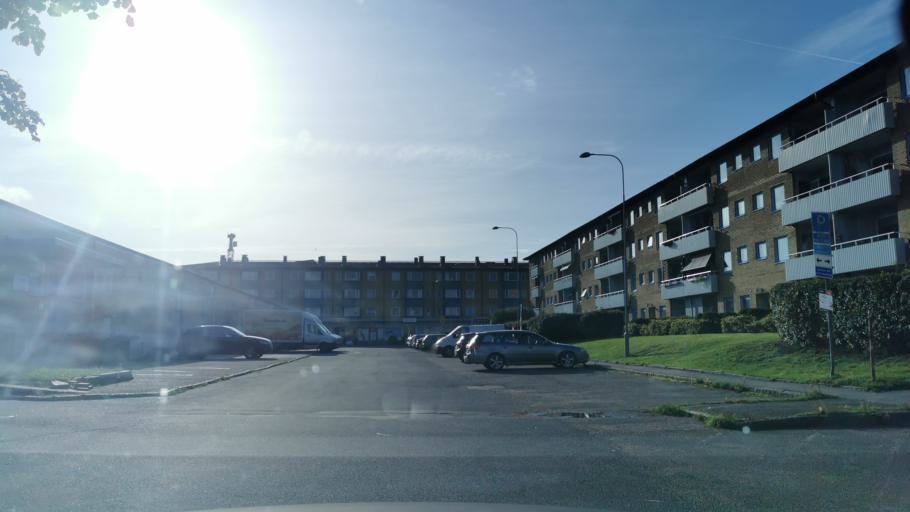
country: SE
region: Vaestra Goetaland
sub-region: Goteborg
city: Majorna
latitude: 57.6639
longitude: 11.9332
